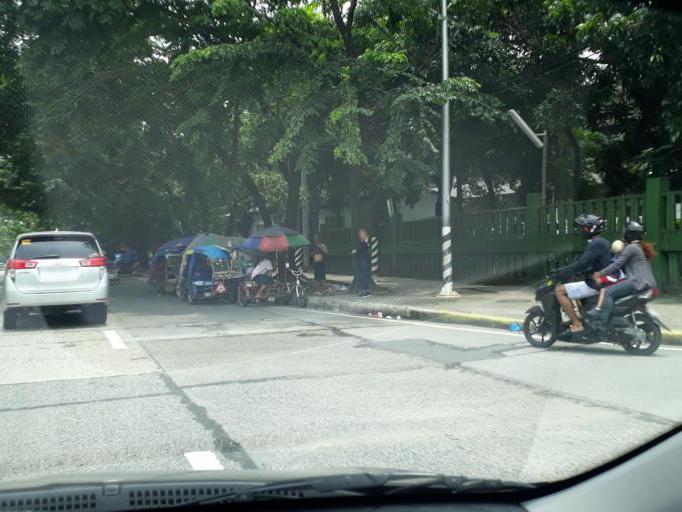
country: PH
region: Metro Manila
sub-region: Quezon City
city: Quezon City
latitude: 14.6466
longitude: 121.0406
